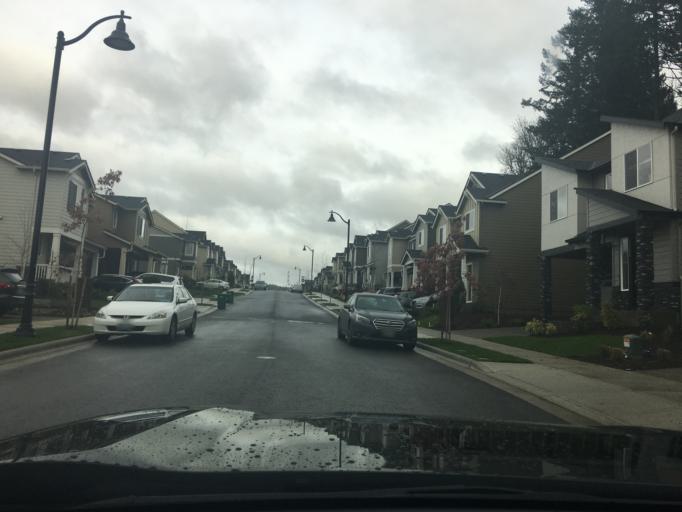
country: US
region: Oregon
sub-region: Washington County
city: Bethany
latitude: 45.5706
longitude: -122.8539
